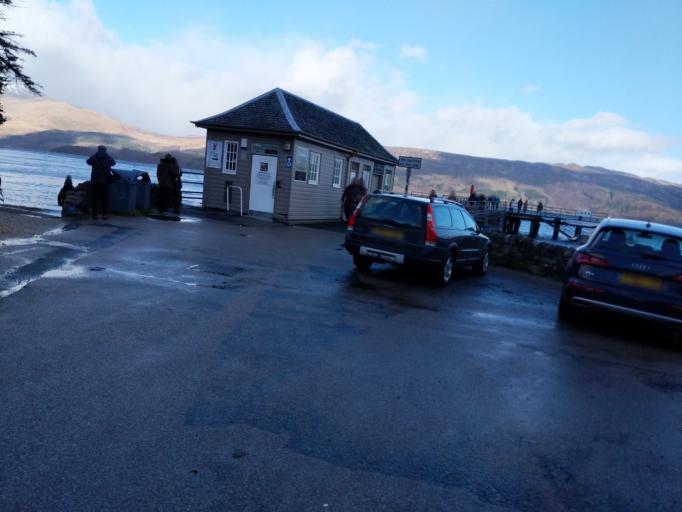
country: GB
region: Scotland
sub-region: West Dunbartonshire
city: Balloch
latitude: 56.1018
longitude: -4.6371
